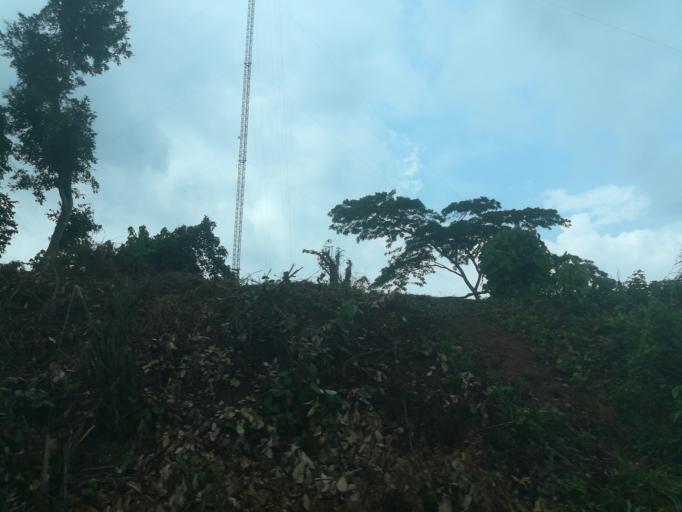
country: NG
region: Lagos
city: Ikorodu
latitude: 6.6636
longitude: 3.6210
